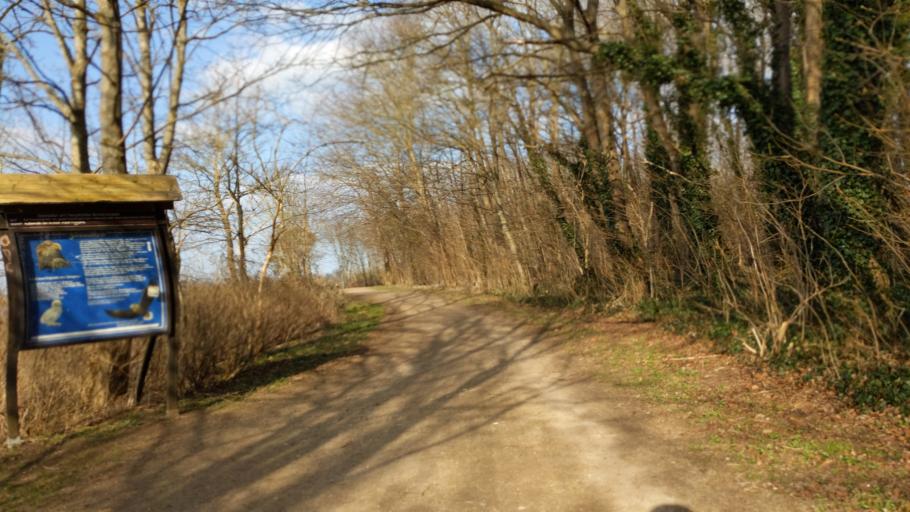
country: DE
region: Schleswig-Holstein
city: Neustadt in Holstein
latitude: 54.1115
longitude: 10.8154
